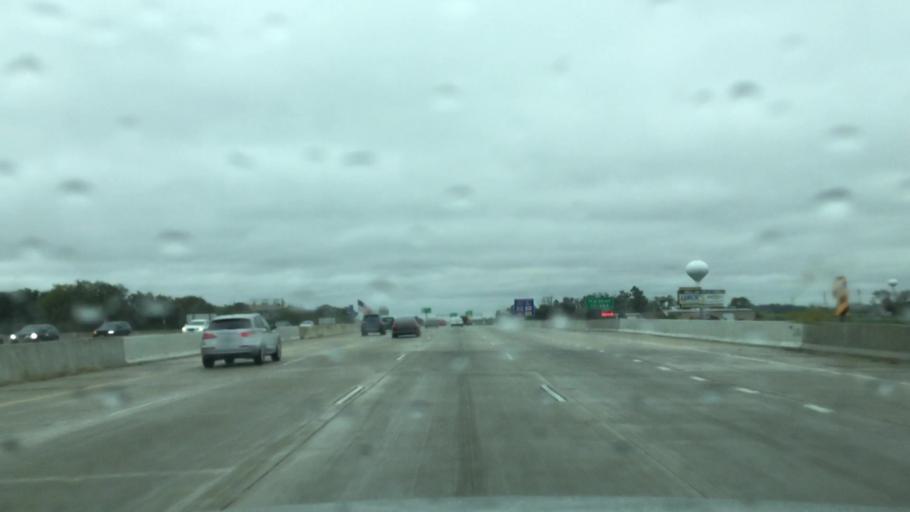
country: US
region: Wisconsin
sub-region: Kenosha County
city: Pleasant Prairie
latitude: 42.5824
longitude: -87.9532
